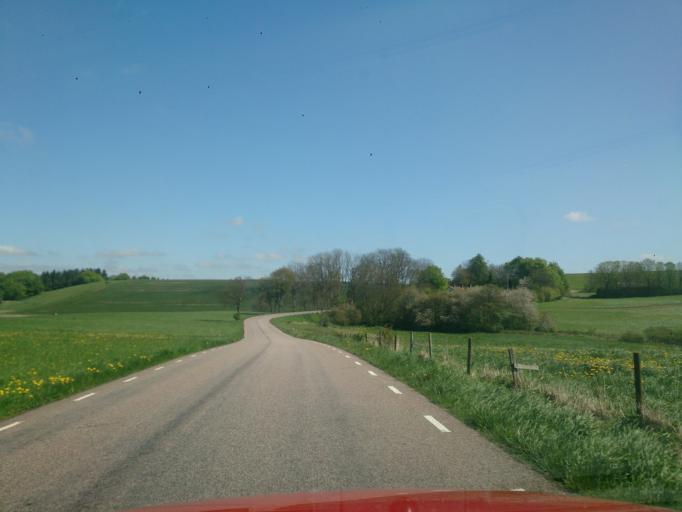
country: SE
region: Skane
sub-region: Ystads Kommun
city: Ystad
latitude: 55.4823
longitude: 13.7302
